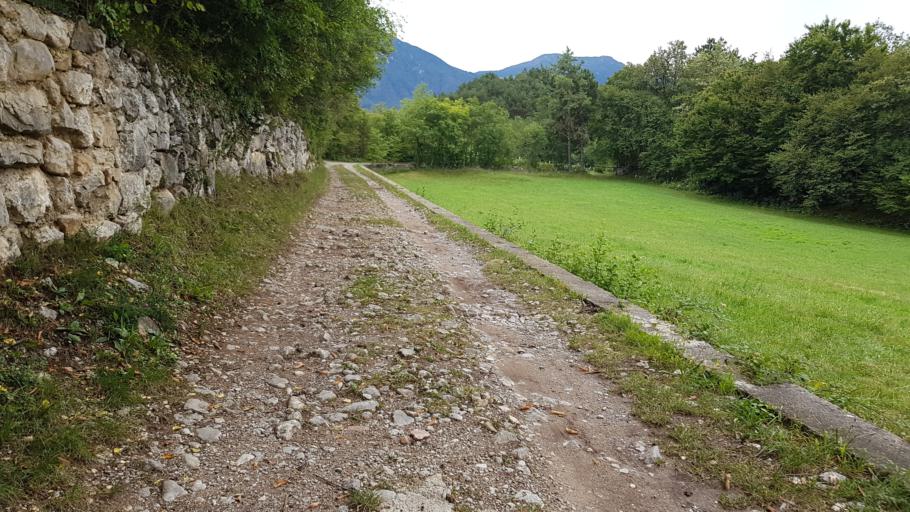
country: IT
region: Trentino-Alto Adige
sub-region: Provincia di Trento
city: Cavedine
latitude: 46.0059
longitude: 10.9718
